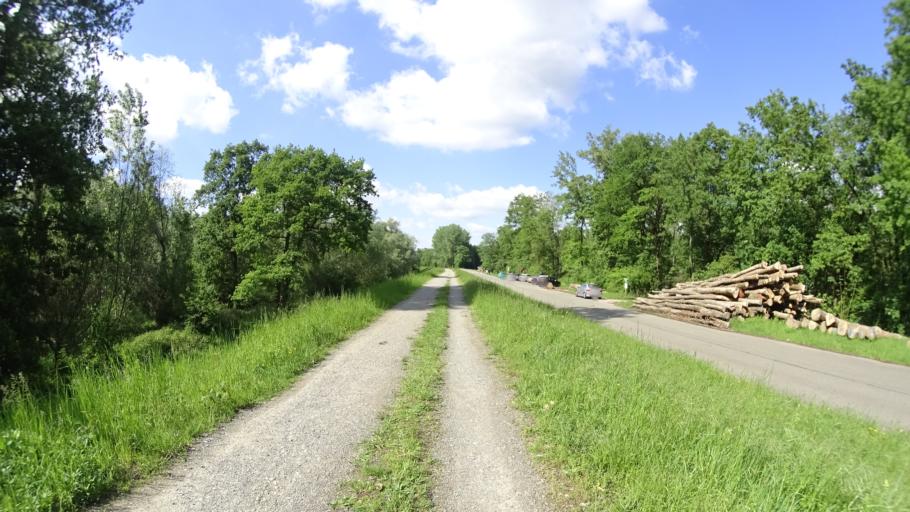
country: DE
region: Baden-Wuerttemberg
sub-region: Karlsruhe Region
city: Rheinstetten
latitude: 49.0179
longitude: 8.3030
